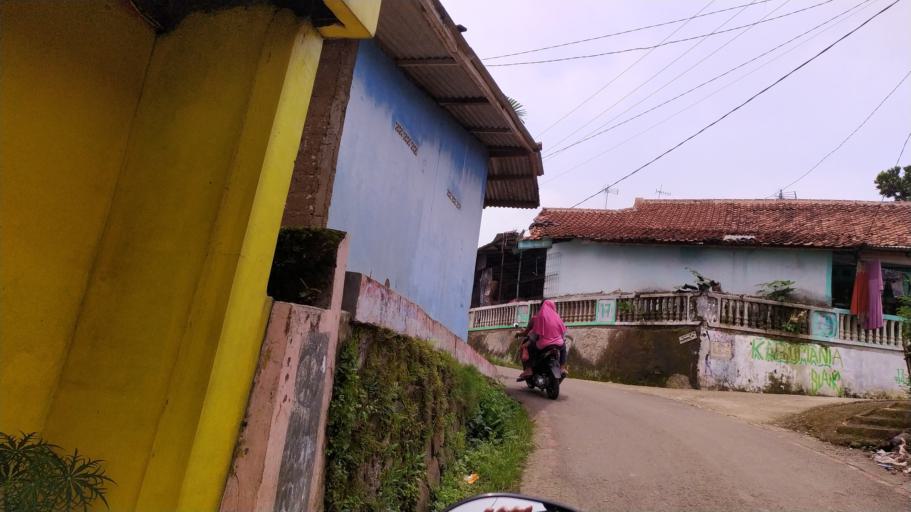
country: ID
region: West Java
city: Ciampea
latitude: -6.6285
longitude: 106.7123
